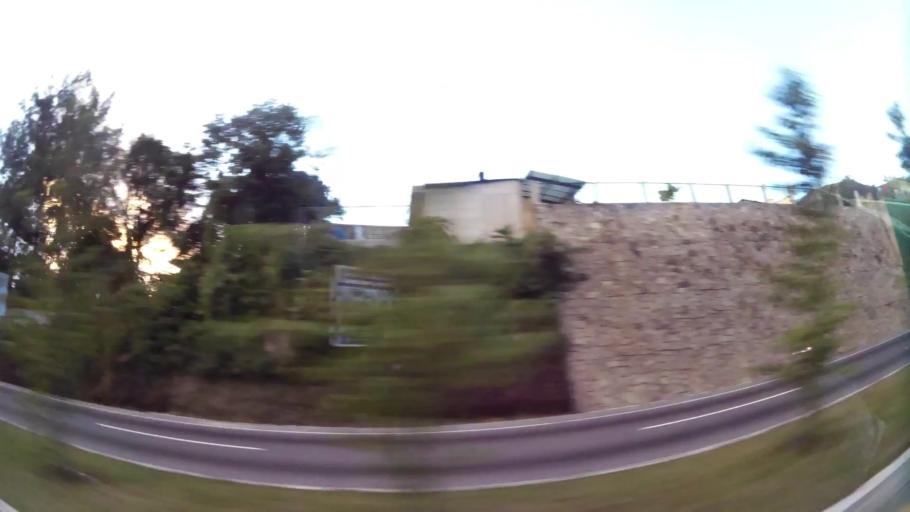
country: GT
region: Sacatepequez
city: San Lucas Sacatepequez
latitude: 14.6111
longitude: -90.6522
